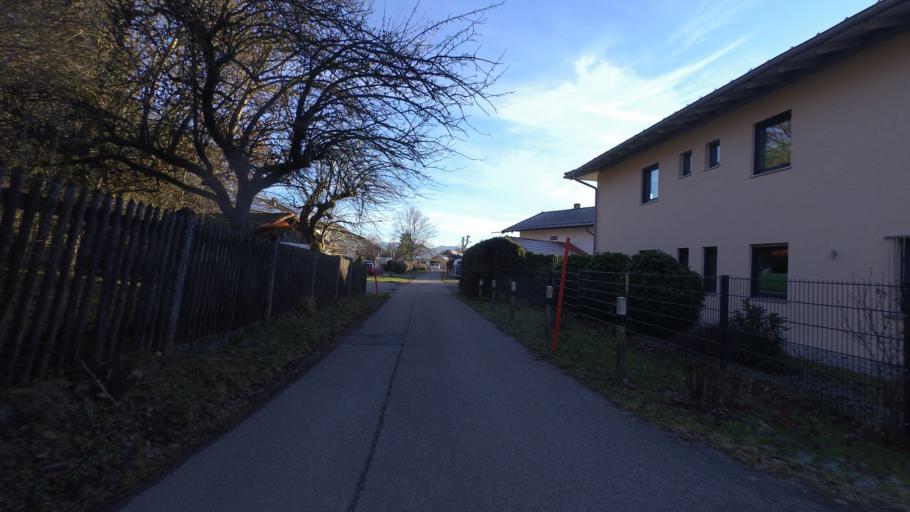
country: DE
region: Bavaria
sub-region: Upper Bavaria
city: Chieming
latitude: 47.9081
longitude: 12.5399
